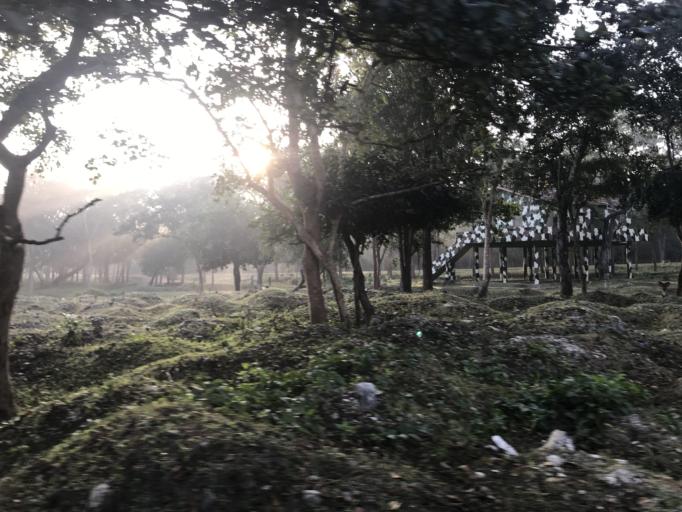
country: IN
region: Karnataka
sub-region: Mysore
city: Heggadadevankote
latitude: 12.0081
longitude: 76.2450
